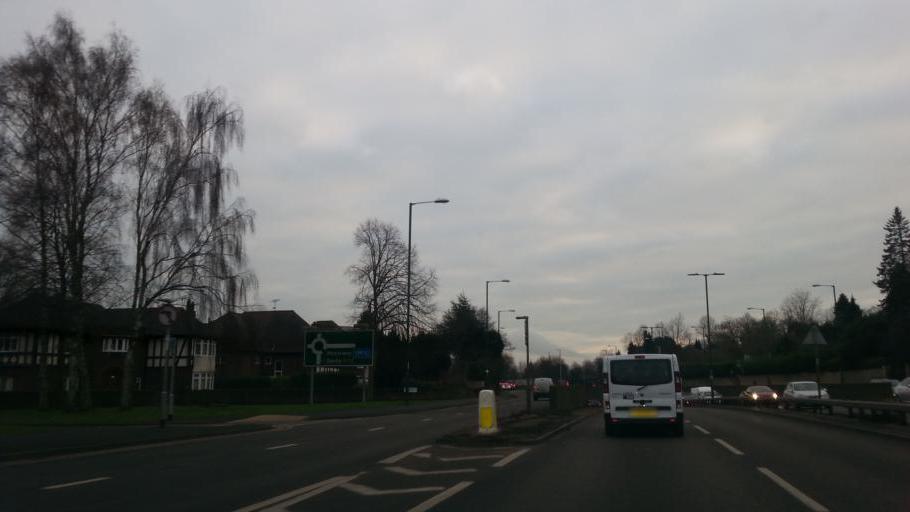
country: GB
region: England
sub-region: Nottingham
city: Nottingham
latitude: 52.9469
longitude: -1.1907
